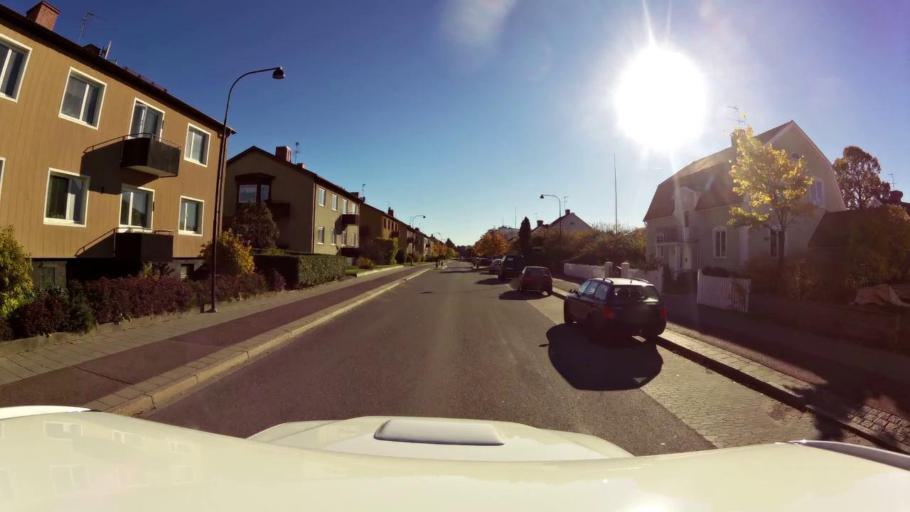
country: SE
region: OEstergoetland
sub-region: Linkopings Kommun
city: Linkoping
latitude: 58.4066
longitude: 15.5980
